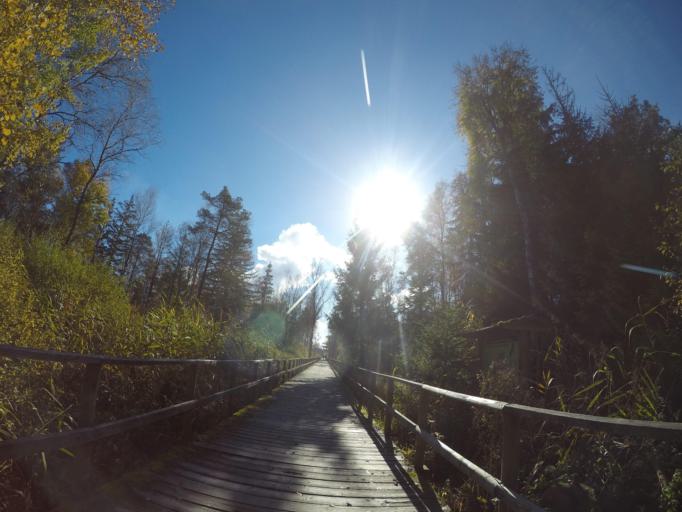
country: DE
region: Baden-Wuerttemberg
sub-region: Tuebingen Region
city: Bad Buchau
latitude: 48.0779
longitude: 9.6026
